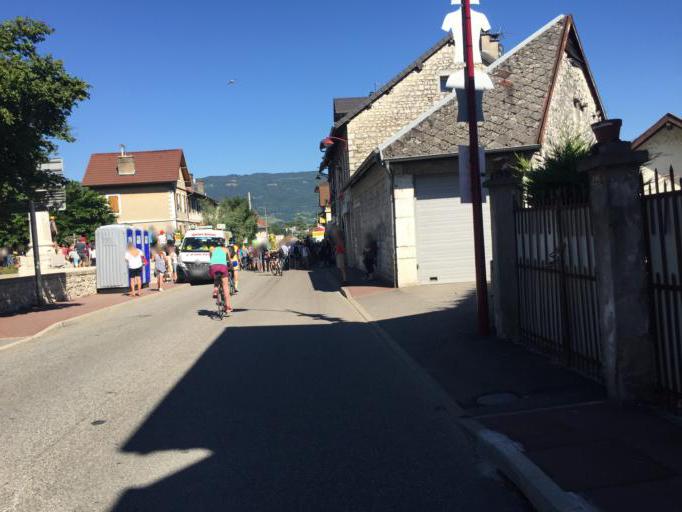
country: FR
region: Rhone-Alpes
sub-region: Departement de l'Ain
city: Culoz
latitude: 45.8480
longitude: 5.7825
